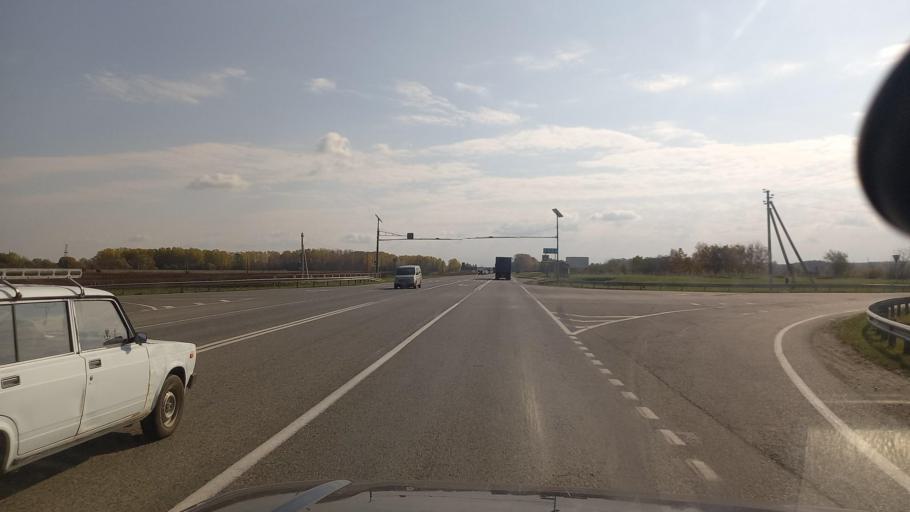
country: RU
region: Krasnodarskiy
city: Novoukrainskiy
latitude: 44.8895
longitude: 38.0746
